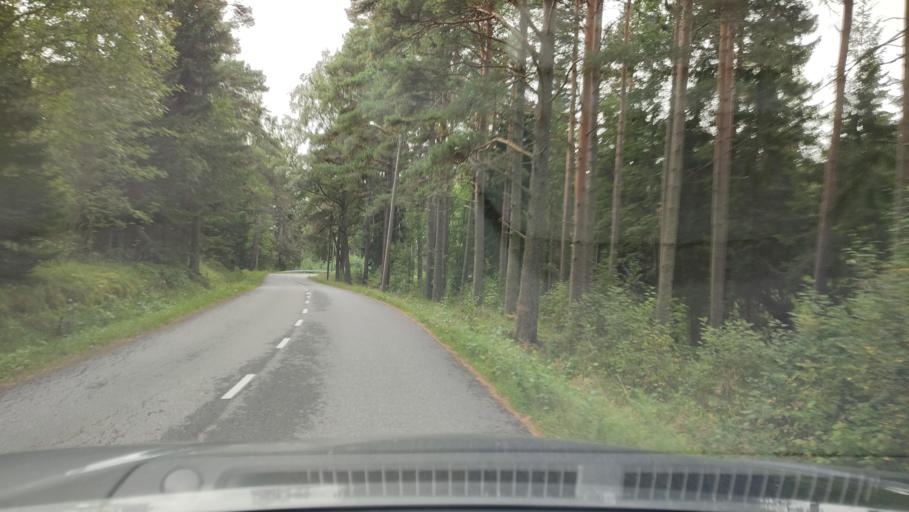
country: FI
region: Ostrobothnia
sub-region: Sydosterbotten
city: Kristinestad
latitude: 62.2765
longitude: 21.3541
